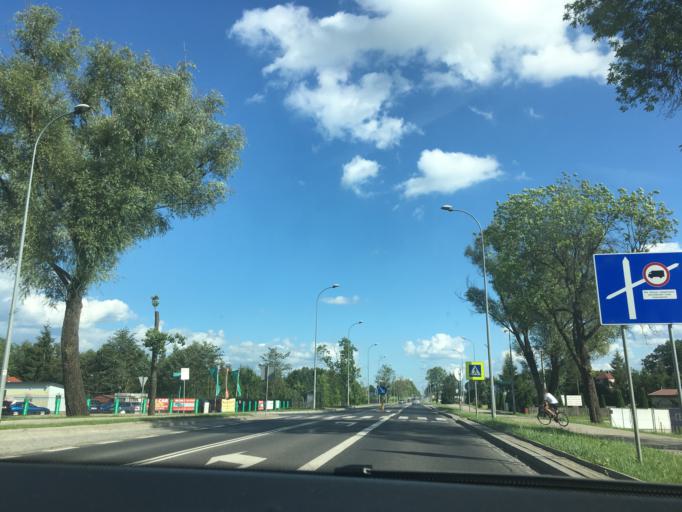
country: PL
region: Podlasie
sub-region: Bialystok
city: Bialystok
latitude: 53.0950
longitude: 23.2361
